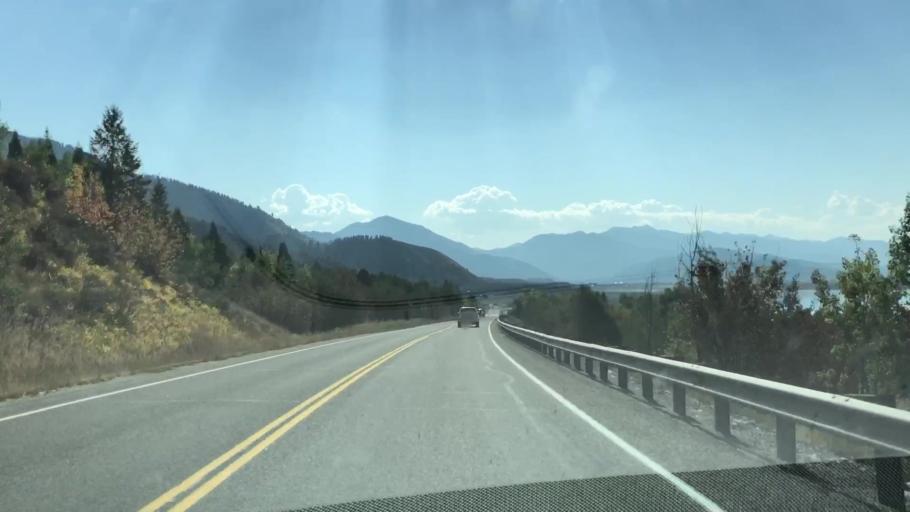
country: US
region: Wyoming
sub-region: Teton County
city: Hoback
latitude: 43.2250
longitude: -111.0788
